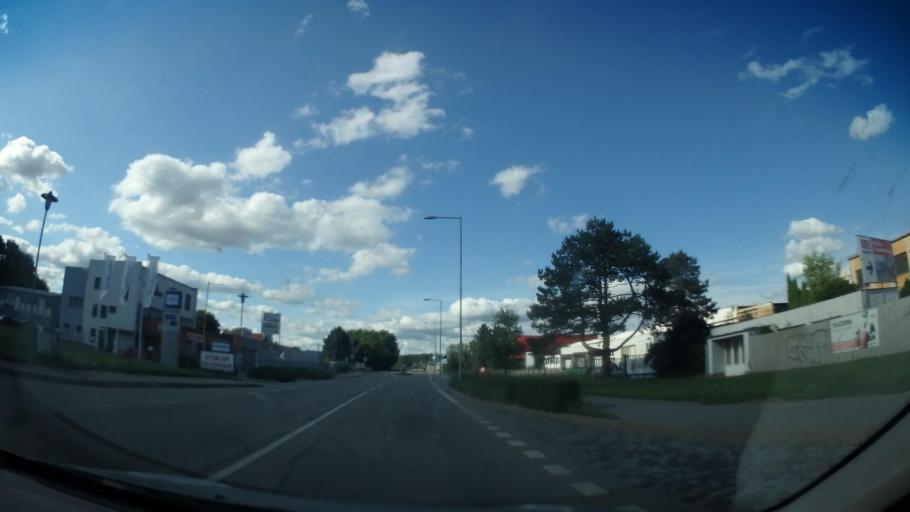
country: CZ
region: South Moravian
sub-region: Okres Blansko
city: Blansko
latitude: 49.3716
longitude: 16.6412
